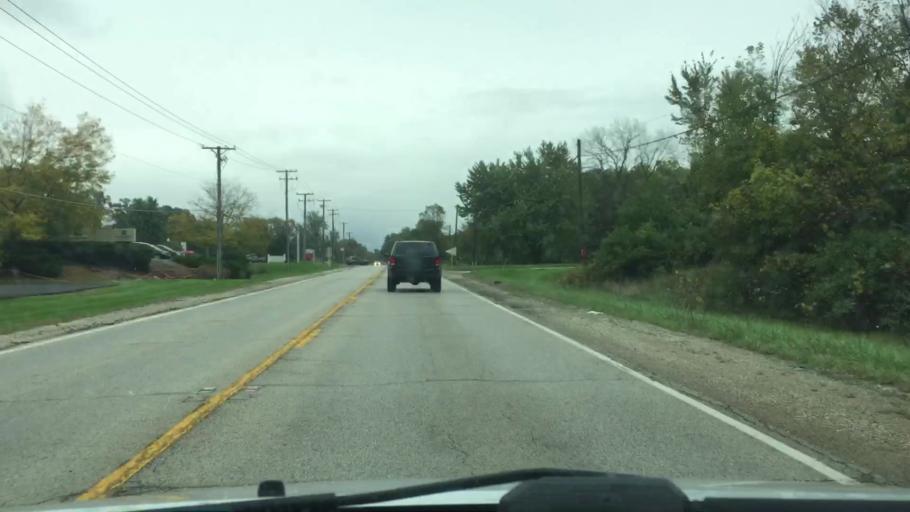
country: US
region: Illinois
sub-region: McHenry County
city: Richmond
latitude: 42.4679
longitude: -88.3069
